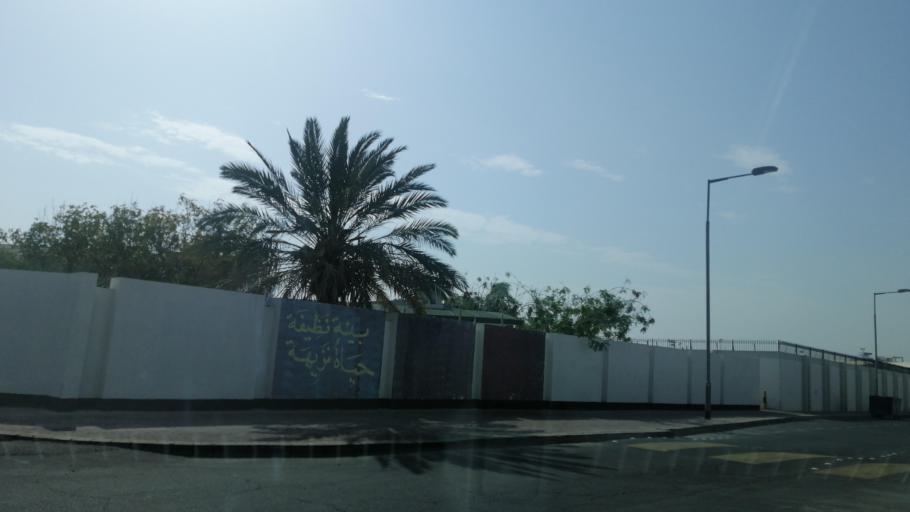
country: BH
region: Muharraq
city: Al Muharraq
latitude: 26.2579
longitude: 50.6303
